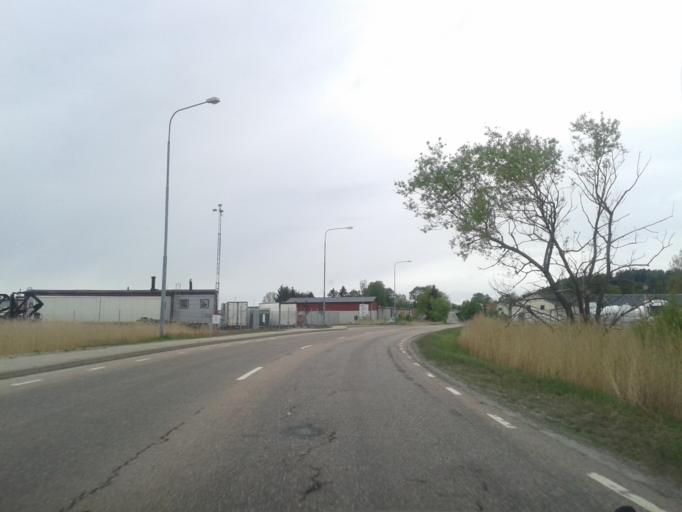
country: SE
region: Vaestra Goetaland
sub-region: Stenungsunds Kommun
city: Stora Hoga
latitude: 58.0203
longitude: 11.8410
